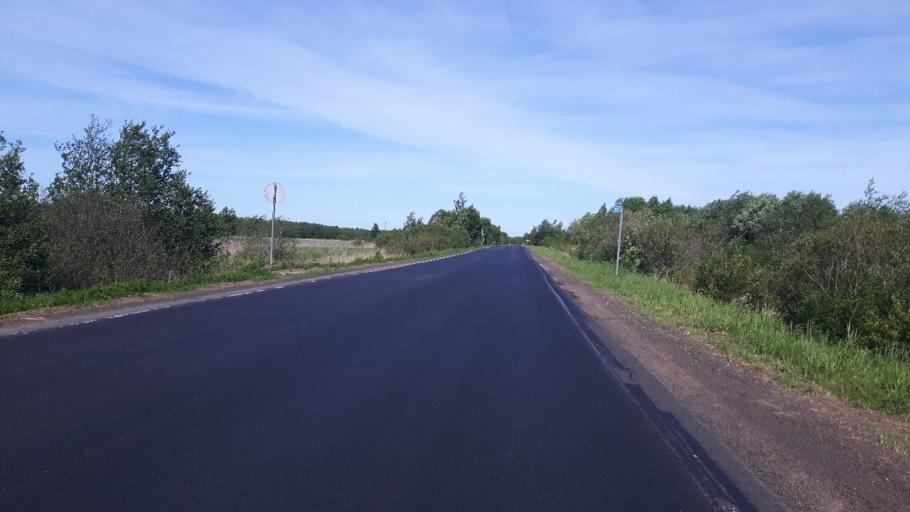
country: RU
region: Leningrad
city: Ivangorod
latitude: 59.4159
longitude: 28.3324
